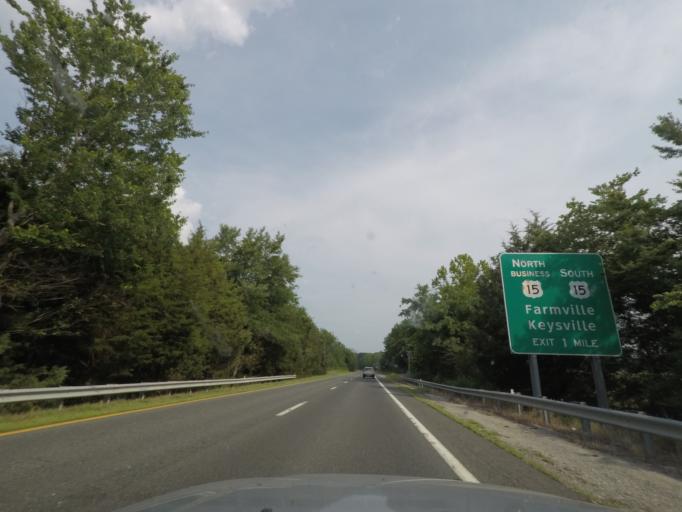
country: US
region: Virginia
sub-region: Prince Edward County
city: Farmville
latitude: 37.2780
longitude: -78.4235
